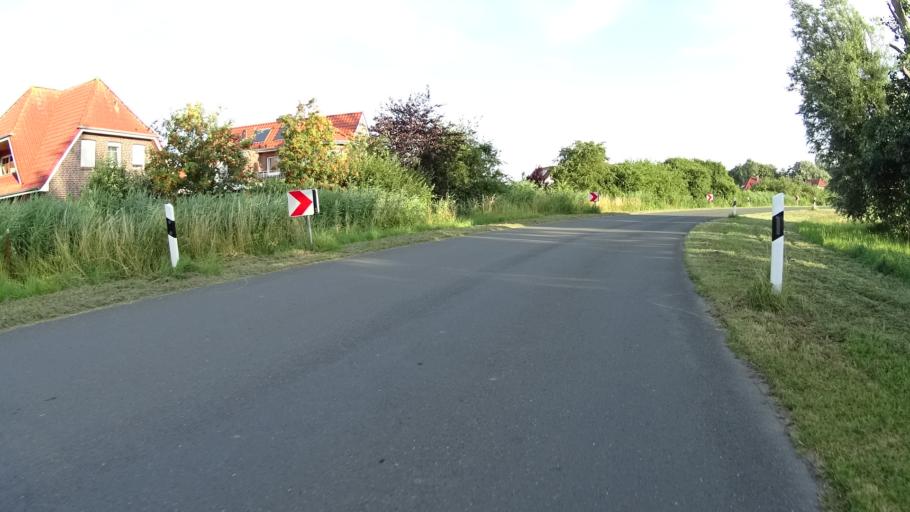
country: DE
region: Lower Saxony
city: Butjadingen
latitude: 53.5963
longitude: 8.3525
